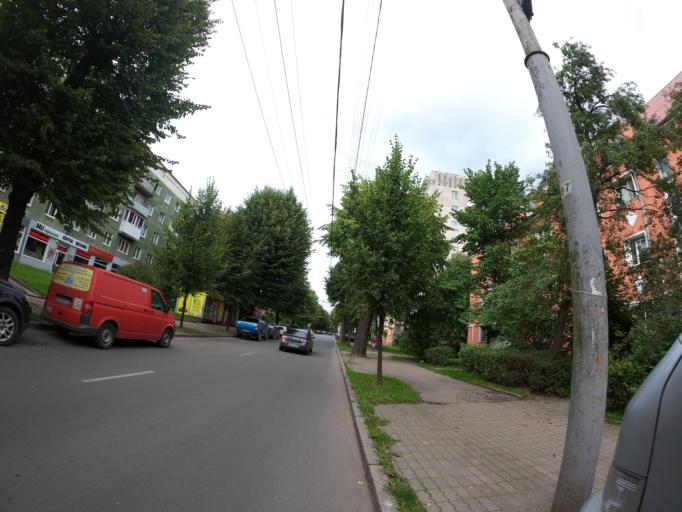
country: RU
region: Kaliningrad
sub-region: Gorod Kaliningrad
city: Kaliningrad
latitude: 54.7235
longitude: 20.4820
